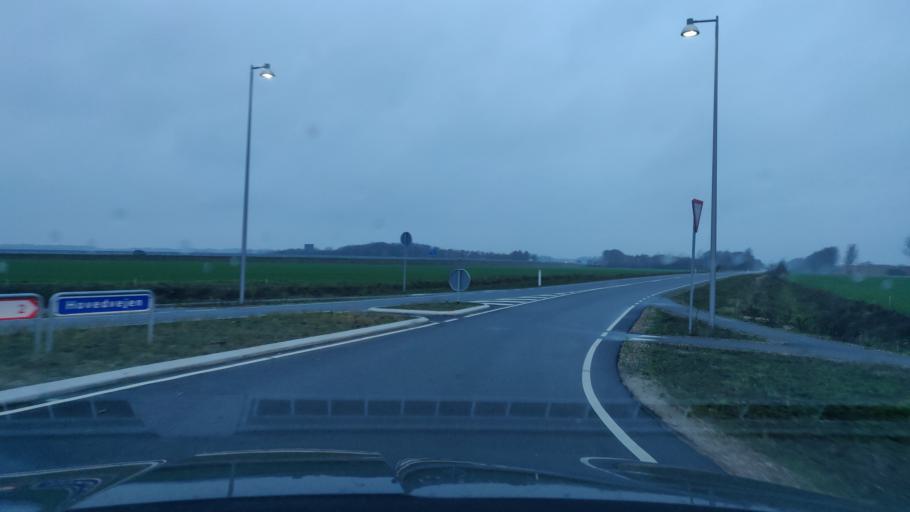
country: DK
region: Central Jutland
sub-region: Herning Kommune
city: Avlum
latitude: 56.2488
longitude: 8.7971
